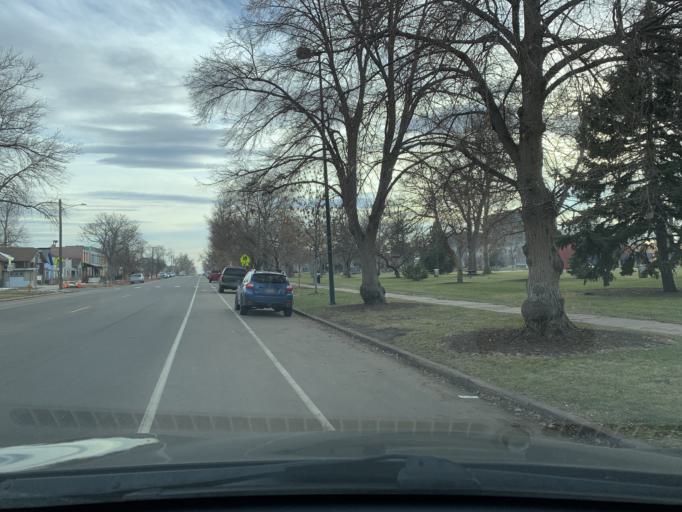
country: US
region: Colorado
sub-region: Denver County
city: Denver
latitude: 39.7359
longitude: -105.0029
